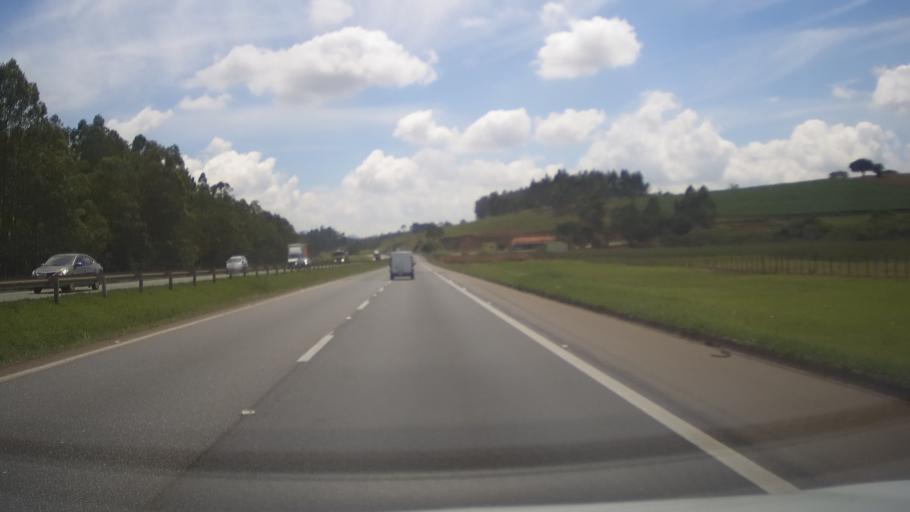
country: BR
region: Minas Gerais
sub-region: Santa Rita Do Sapucai
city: Santa Rita do Sapucai
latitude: -22.0959
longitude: -45.7143
